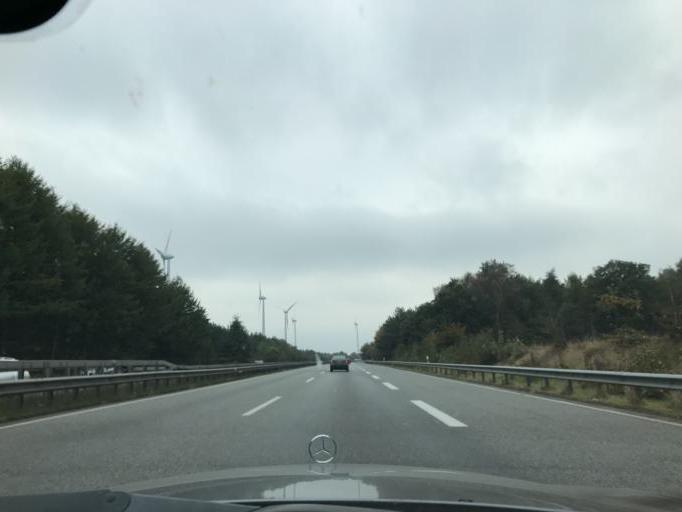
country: DE
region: Lower Saxony
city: Hatten
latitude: 53.0586
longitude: 8.4180
